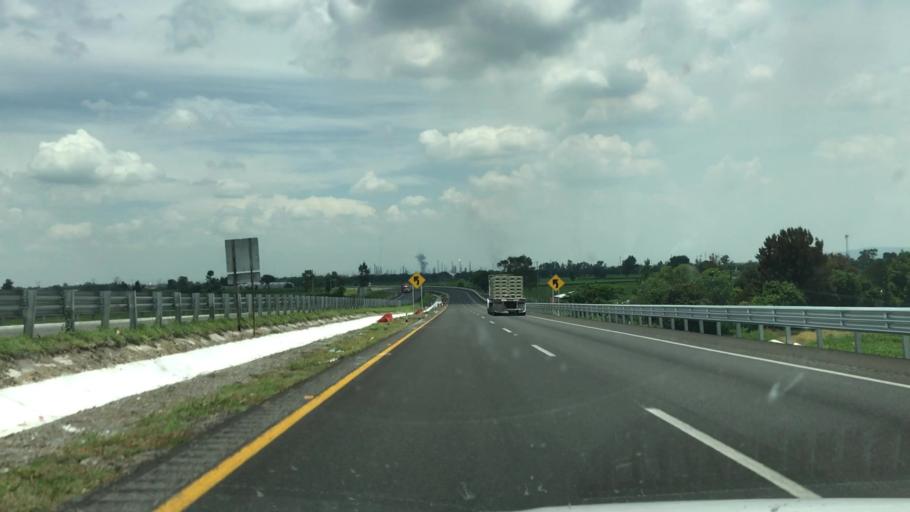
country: MX
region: Guanajuato
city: Salamanca
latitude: 20.6064
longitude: -101.2121
